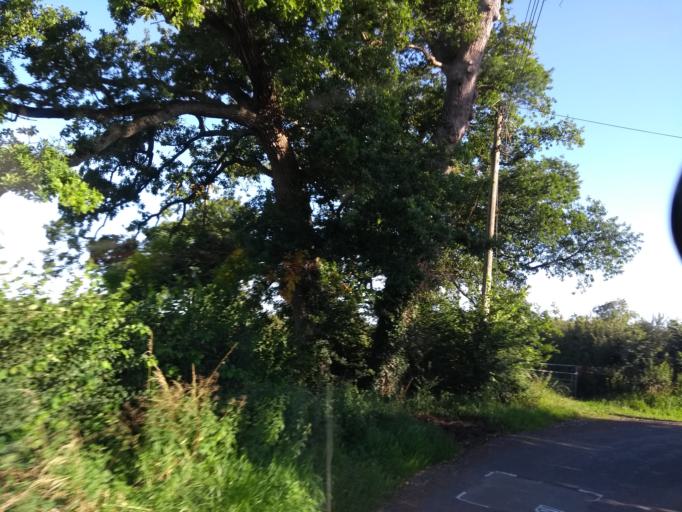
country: GB
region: England
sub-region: Somerset
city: Axbridge
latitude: 51.2592
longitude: -2.8562
